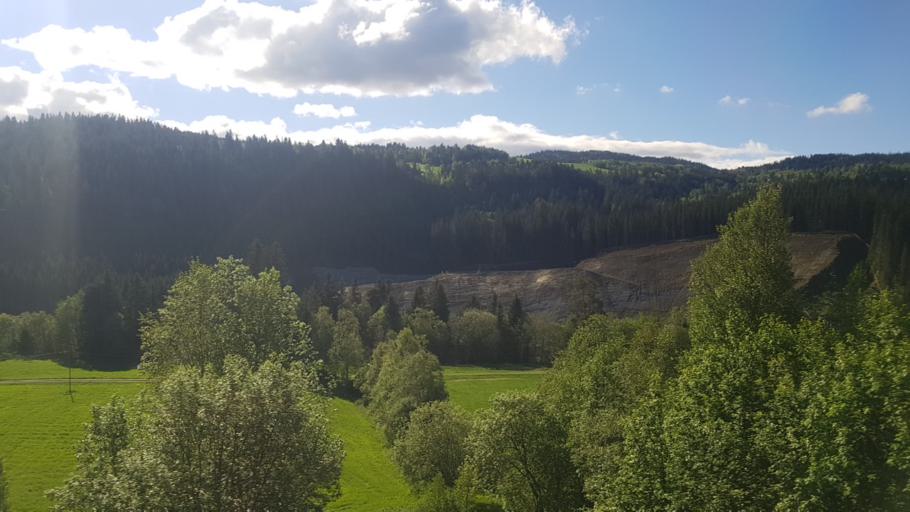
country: NO
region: Sor-Trondelag
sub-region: Midtre Gauldal
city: Storen
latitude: 62.9759
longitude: 10.2167
